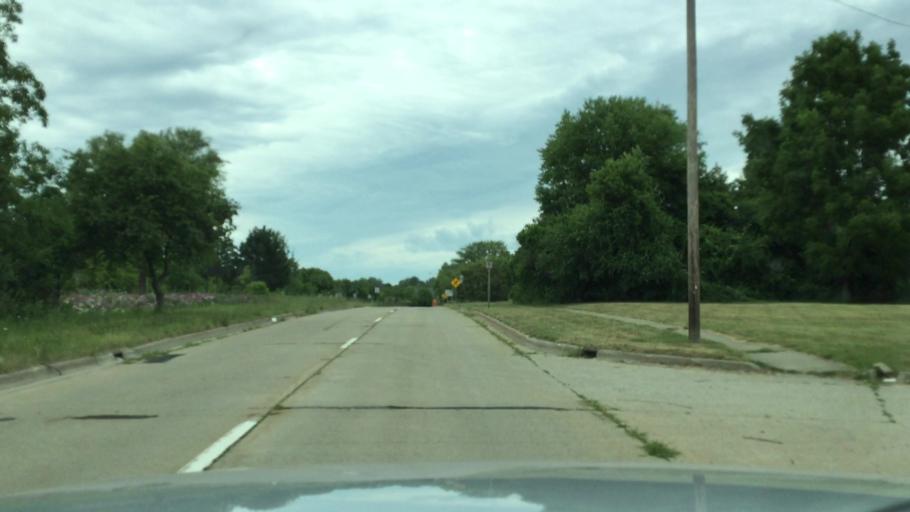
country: US
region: Michigan
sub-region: Genesee County
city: Beecher
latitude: 43.0816
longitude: -83.6843
